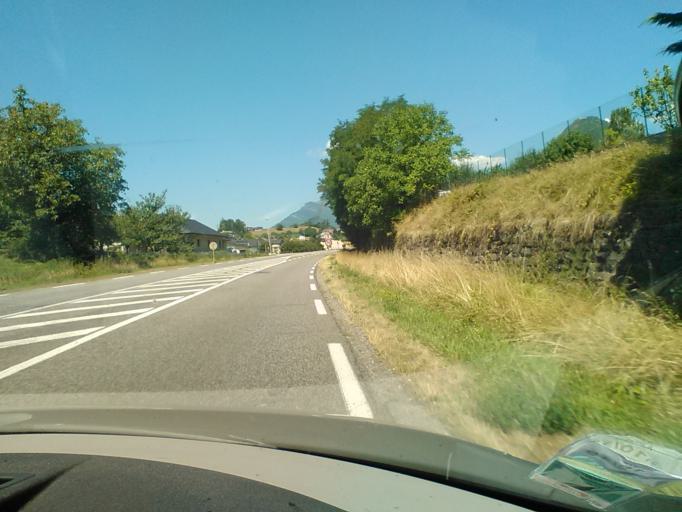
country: FR
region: Rhone-Alpes
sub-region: Departement de la Savoie
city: Les Marches
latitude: 45.5259
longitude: 5.9934
